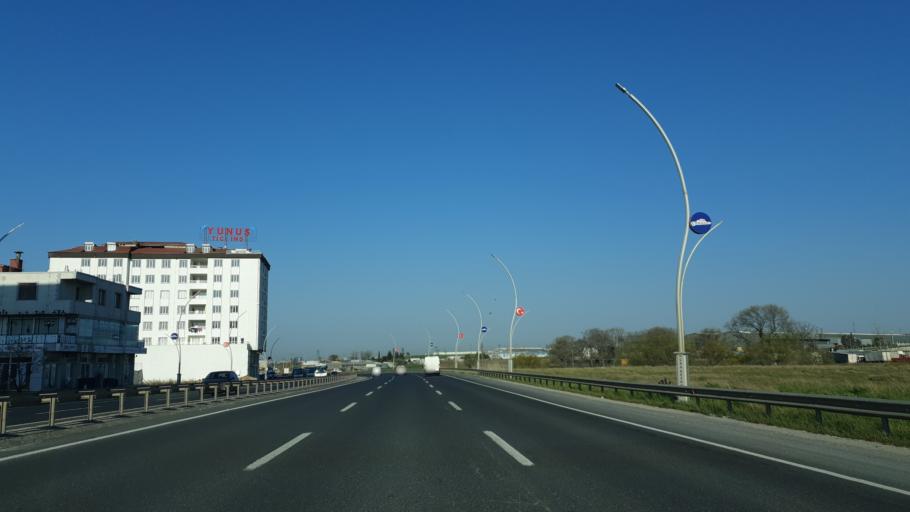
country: TR
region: Tekirdag
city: Cerkezkoey
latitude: 41.2731
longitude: 27.9704
